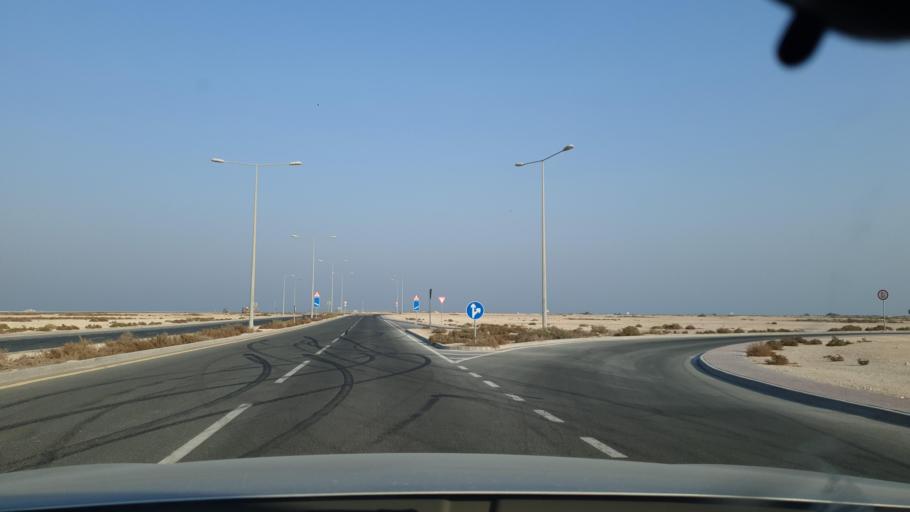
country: QA
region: Al Wakrah
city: Al Wakrah
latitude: 25.1944
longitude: 51.6139
